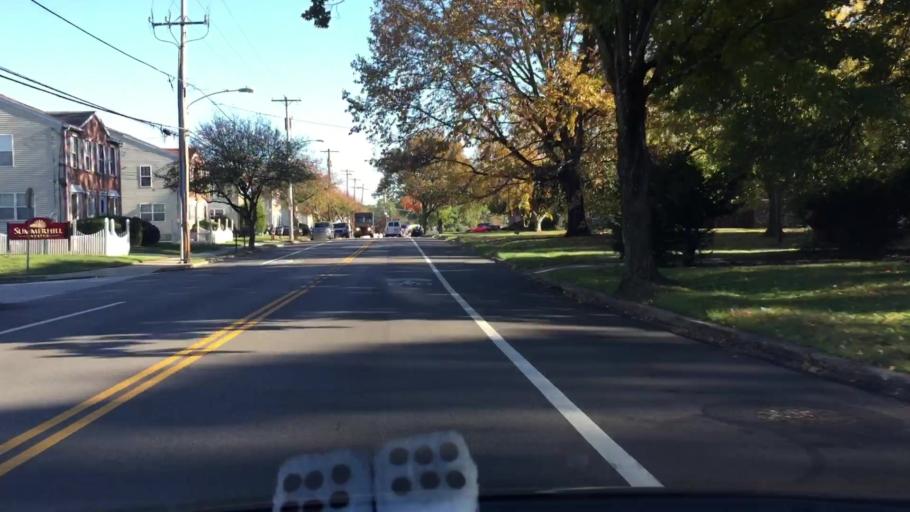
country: US
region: New Jersey
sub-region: Burlington County
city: Riverton
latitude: 40.0651
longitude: -75.0245
